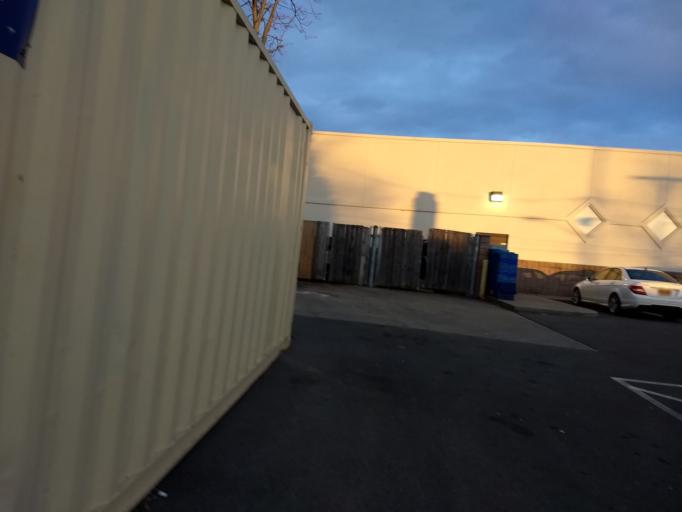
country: US
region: New York
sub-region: Onondaga County
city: Lyncourt
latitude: 43.0725
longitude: -76.1420
